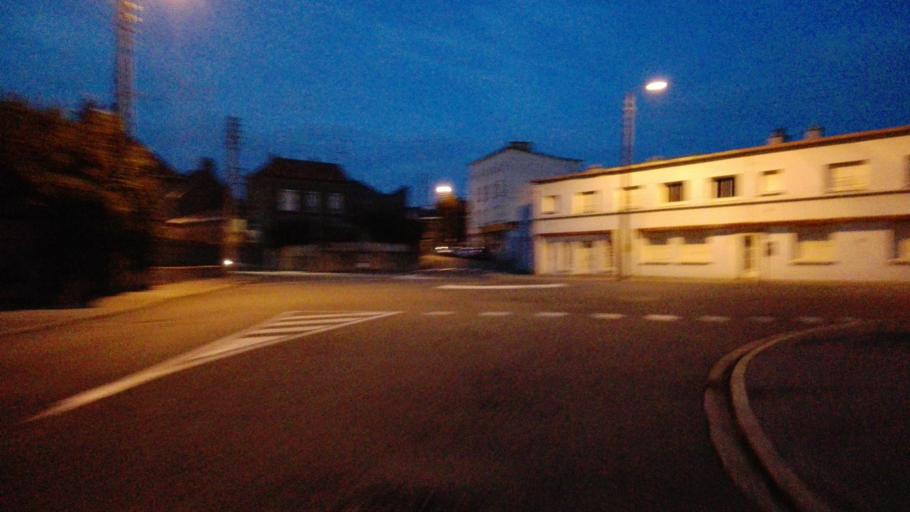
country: FR
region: Nord-Pas-de-Calais
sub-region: Departement du Pas-de-Calais
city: Boulogne-sur-Mer
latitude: 50.7135
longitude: 1.6112
